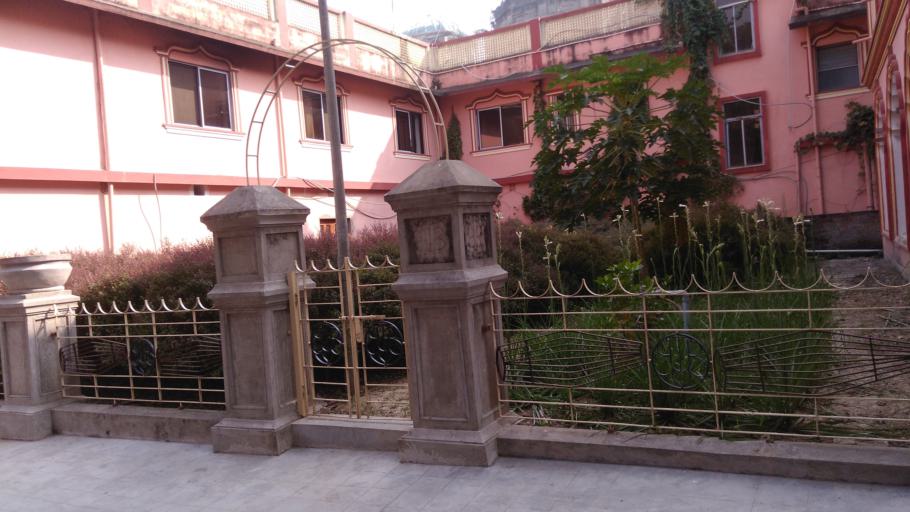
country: IN
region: West Bengal
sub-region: Nadia
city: Navadwip
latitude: 23.4261
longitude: 88.3889
